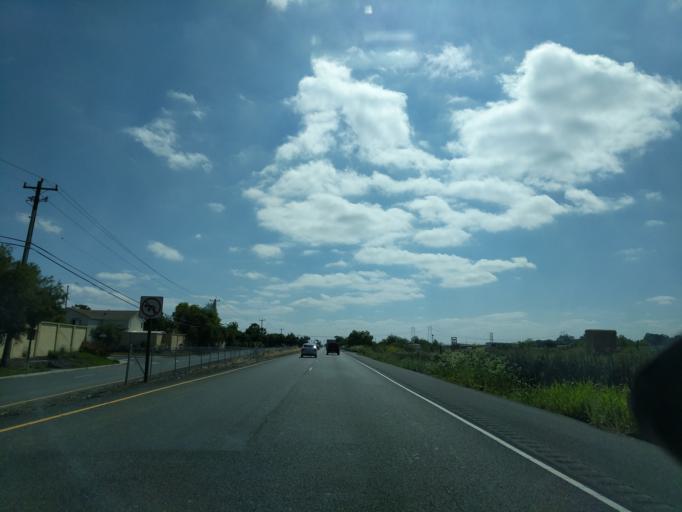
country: US
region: California
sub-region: Contra Costa County
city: Byron
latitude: 37.8893
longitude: -121.6301
